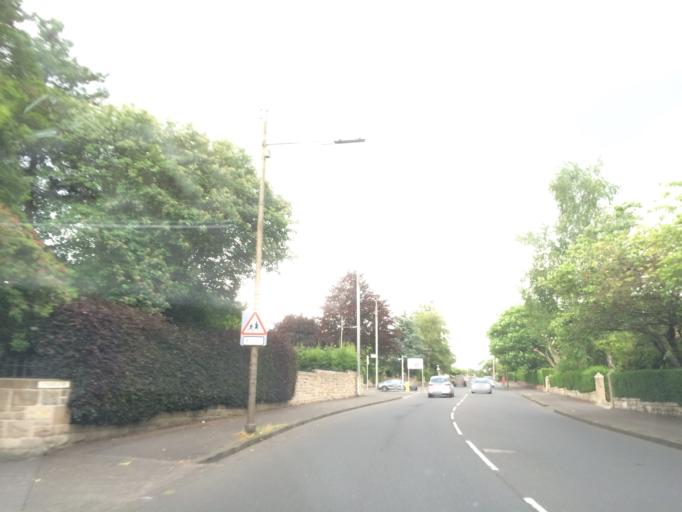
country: GB
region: Scotland
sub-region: East Renfrewshire
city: Giffnock
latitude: 55.8132
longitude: -4.2780
